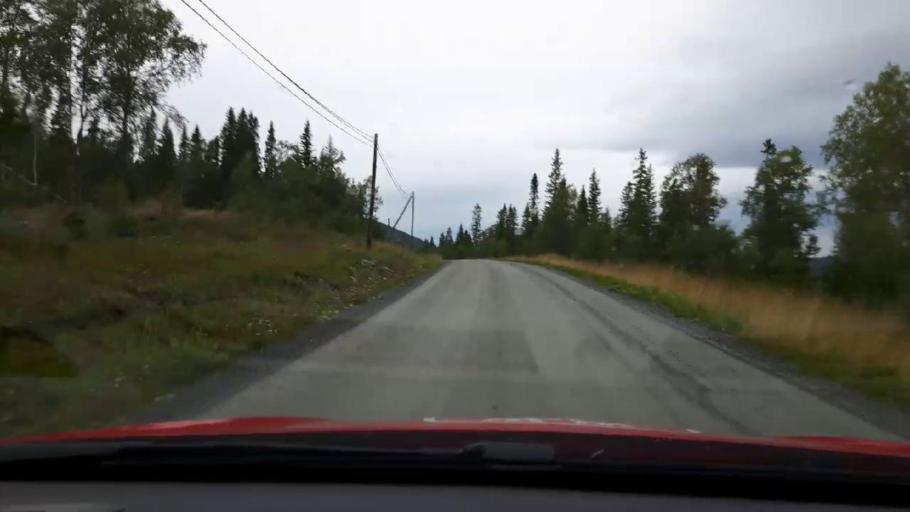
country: SE
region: Jaemtland
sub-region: Are Kommun
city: Are
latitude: 63.4841
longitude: 13.1460
